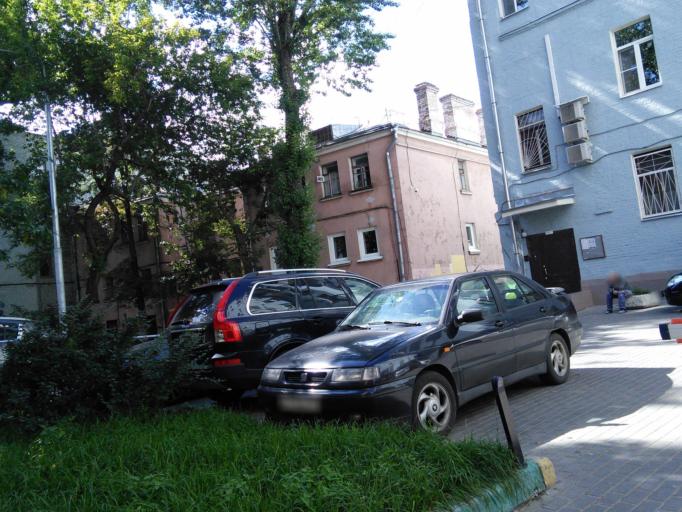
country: RU
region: Moscow
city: Moscow
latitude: 55.7591
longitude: 37.6354
